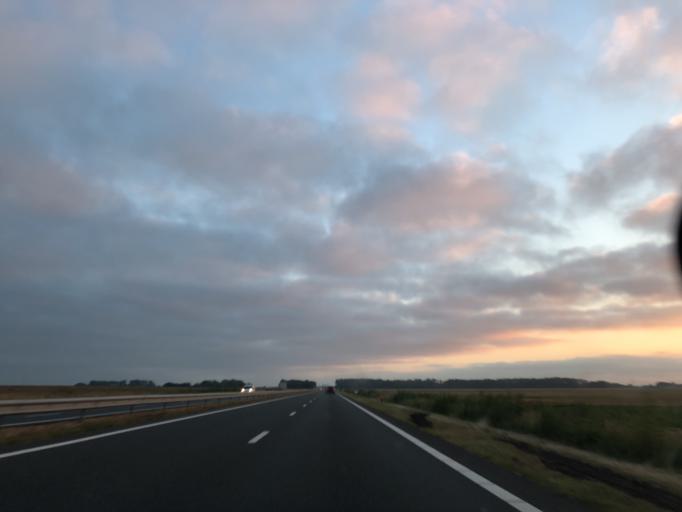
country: NL
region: Groningen
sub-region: Gemeente Veendam
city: Veendam
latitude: 53.1483
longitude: 6.8971
